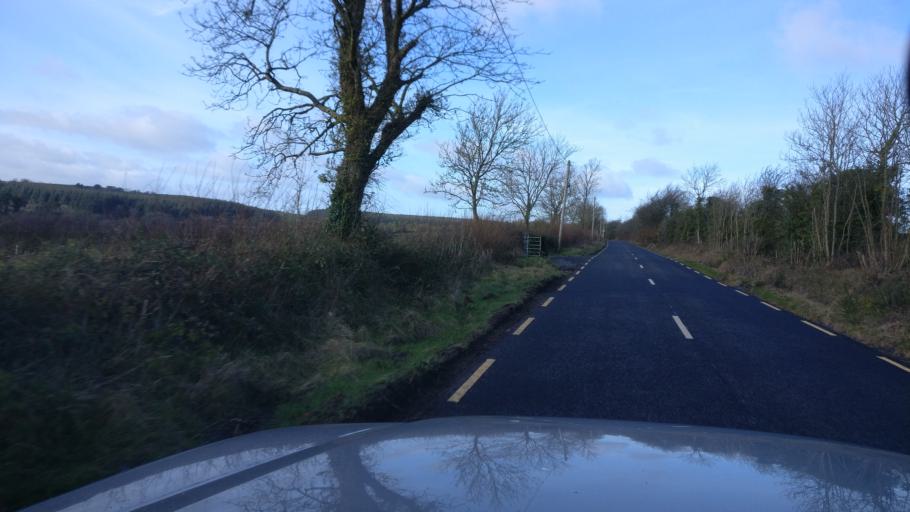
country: IE
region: Leinster
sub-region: Kilkenny
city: Castlecomer
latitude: 52.8992
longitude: -7.1748
